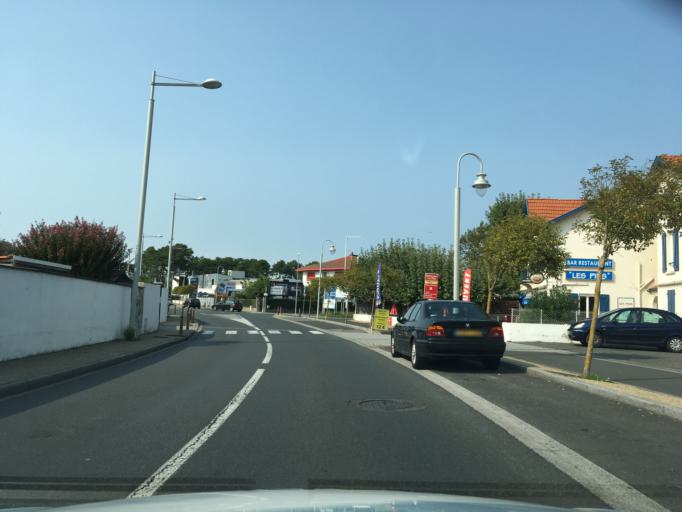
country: FR
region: Aquitaine
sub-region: Departement des Pyrenees-Atlantiques
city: Boucau
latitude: 43.5194
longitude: -1.5018
